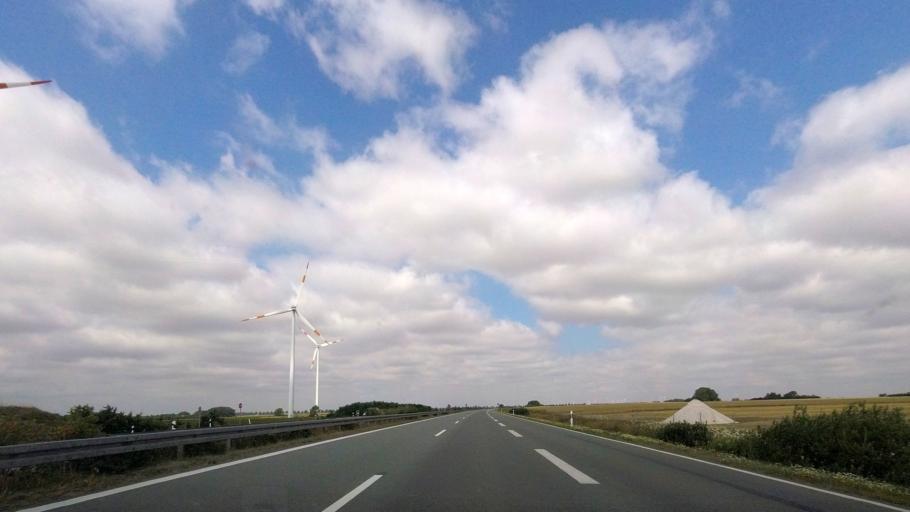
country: DE
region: Mecklenburg-Vorpommern
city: Gormin
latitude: 53.9983
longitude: 13.3162
